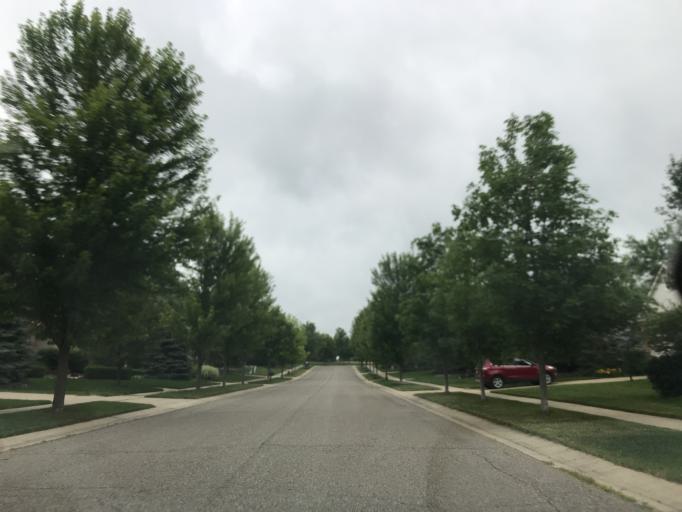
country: US
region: Michigan
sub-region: Oakland County
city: South Lyon
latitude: 42.4820
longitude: -83.6489
